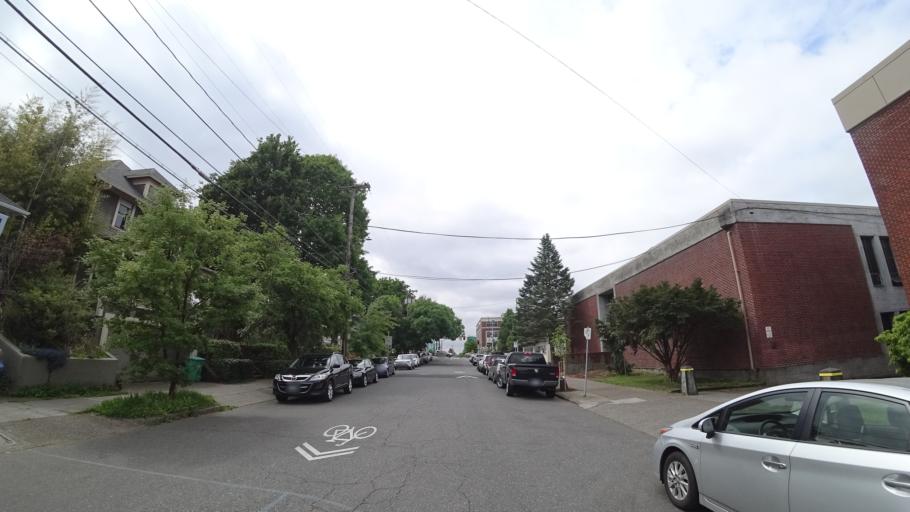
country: US
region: Oregon
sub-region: Multnomah County
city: Portland
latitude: 45.4987
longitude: -122.6376
